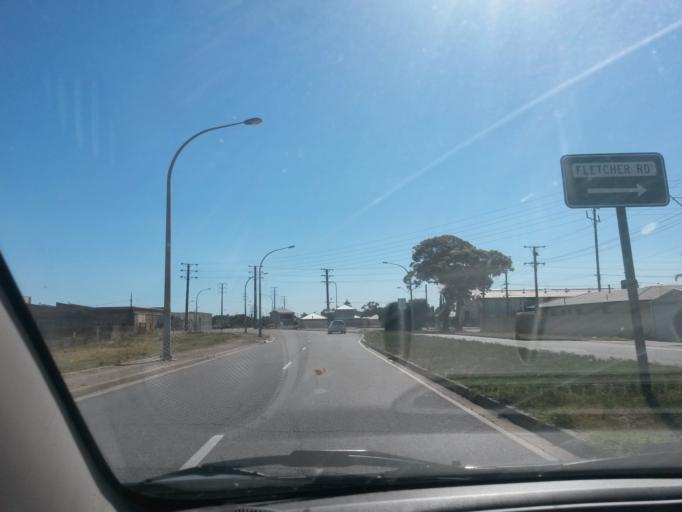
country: AU
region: South Australia
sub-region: Port Adelaide Enfield
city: Birkenhead
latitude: -34.8395
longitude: 138.4997
